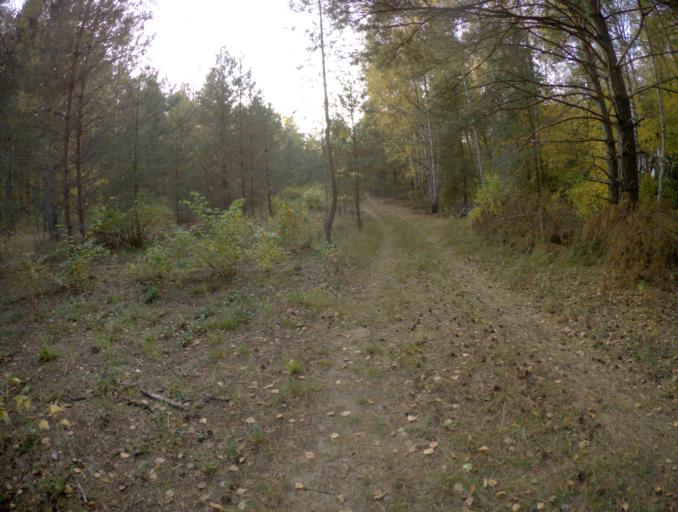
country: RU
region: Vladimir
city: Raduzhnyy
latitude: 56.0234
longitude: 40.2806
